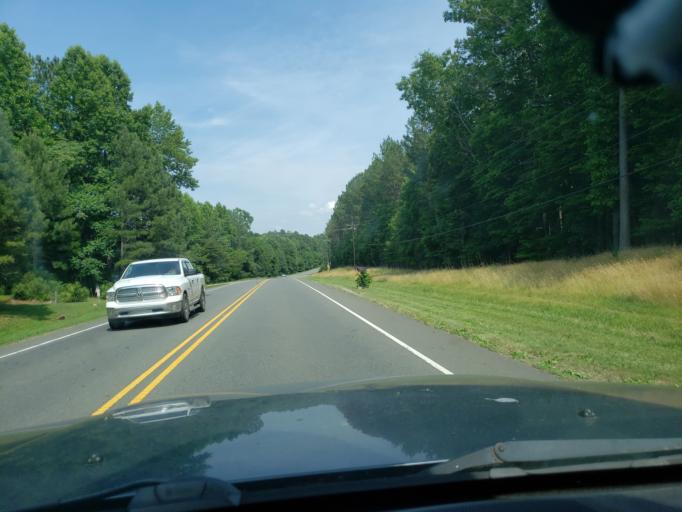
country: US
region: North Carolina
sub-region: Alamance County
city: Saxapahaw
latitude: 35.9320
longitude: -79.2105
